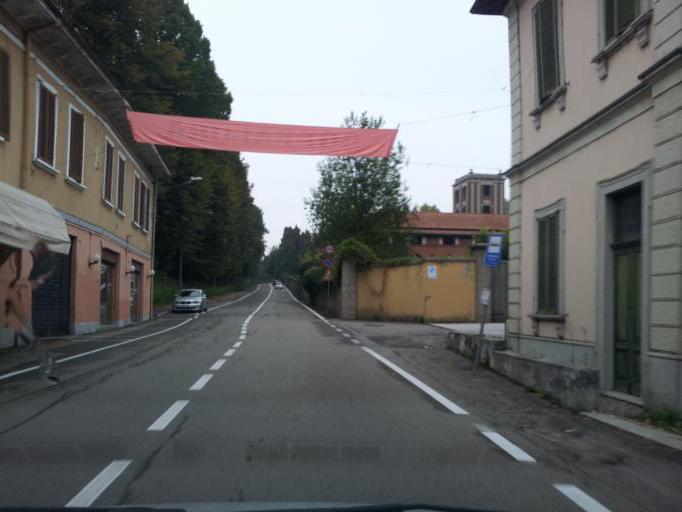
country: IT
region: Lombardy
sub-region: Provincia di Varese
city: Varano Borghi
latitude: 45.7690
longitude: 8.7052
